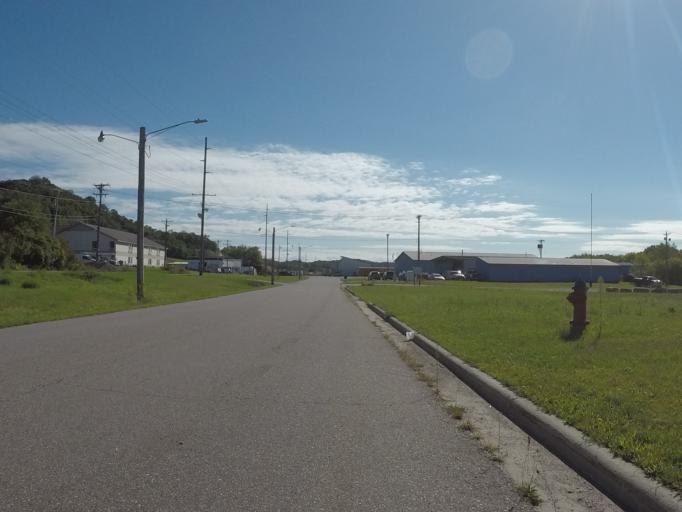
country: US
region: Wisconsin
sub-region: Richland County
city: Richland Center
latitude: 43.3193
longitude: -90.3735
